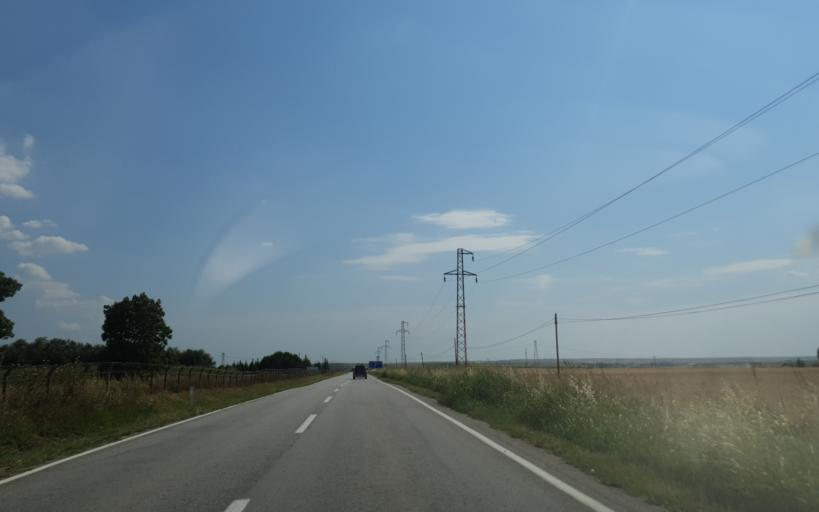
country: TR
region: Kirklareli
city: Buyukkaristiran
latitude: 41.3130
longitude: 27.5177
